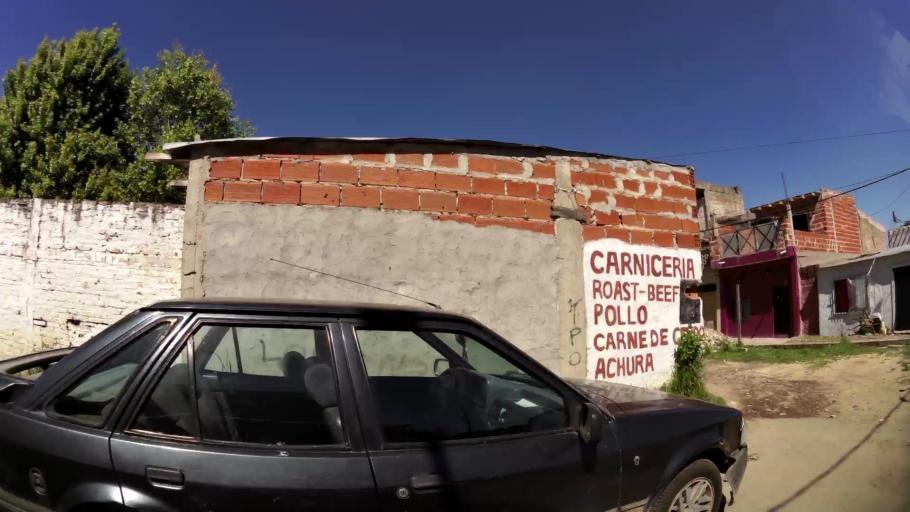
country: AR
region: Buenos Aires
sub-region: Partido de Quilmes
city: Quilmes
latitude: -34.7059
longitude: -58.3011
